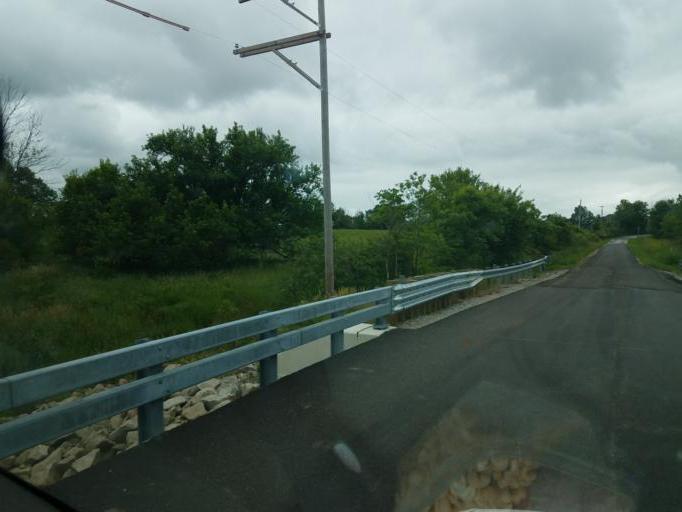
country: US
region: Ohio
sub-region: Morrow County
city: Cardington
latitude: 40.5468
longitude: -82.9139
